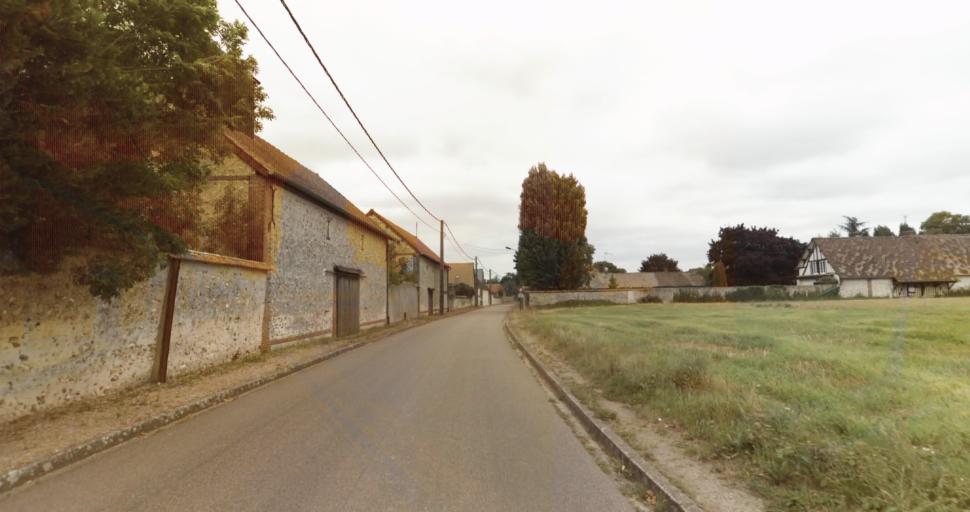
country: FR
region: Haute-Normandie
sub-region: Departement de l'Eure
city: La Couture-Boussey
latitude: 48.9086
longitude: 1.3475
